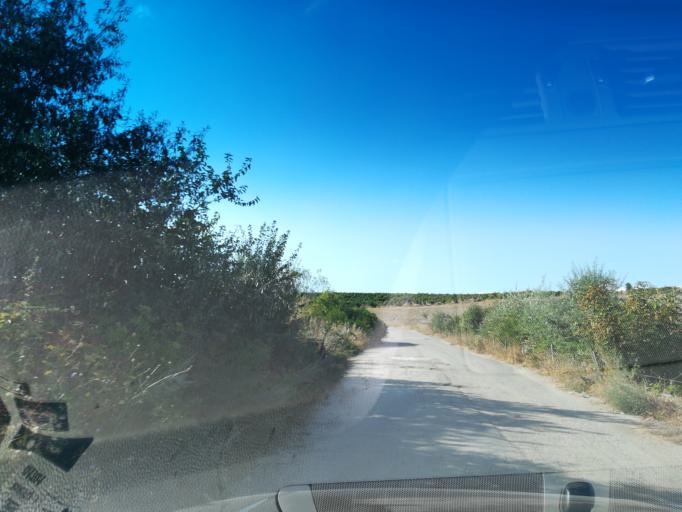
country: BG
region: Khaskovo
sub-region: Obshtina Mineralni Bani
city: Mineralni Bani
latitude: 41.9715
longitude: 25.3498
